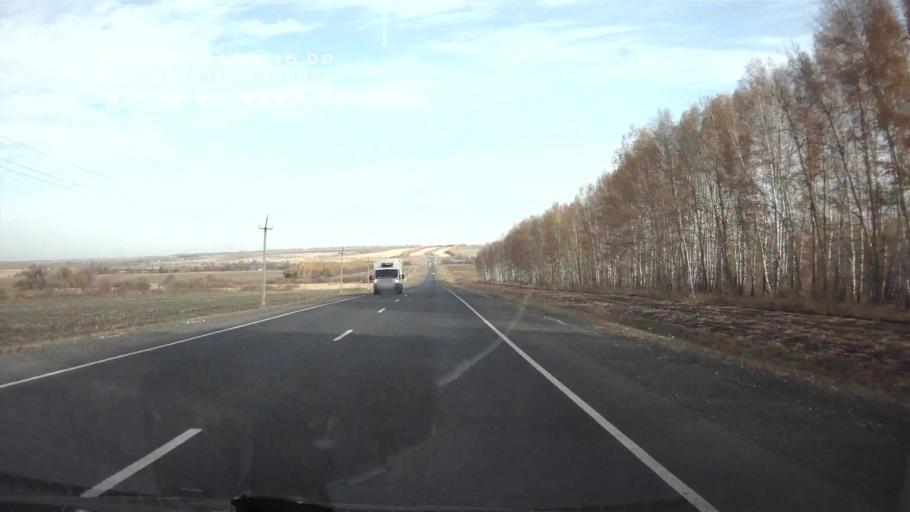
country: RU
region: Penza
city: Mokshan
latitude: 53.5991
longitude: 44.7250
